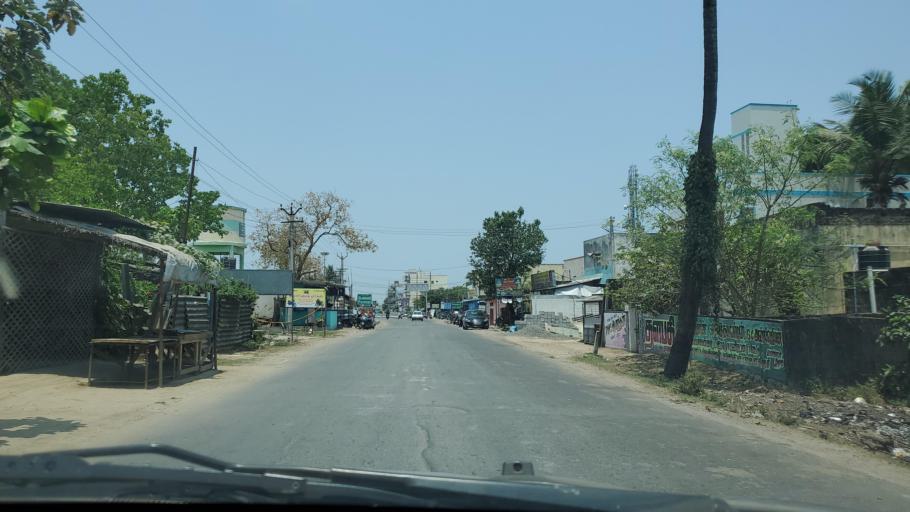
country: IN
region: Tamil Nadu
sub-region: Kancheepuram
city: Vengavasal
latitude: 12.8557
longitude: 80.1719
